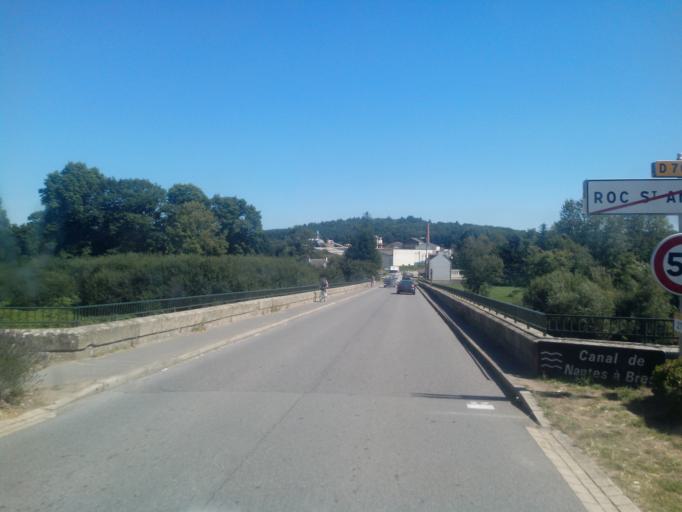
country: FR
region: Brittany
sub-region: Departement du Morbihan
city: Guillac
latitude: 47.8654
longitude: -2.4461
